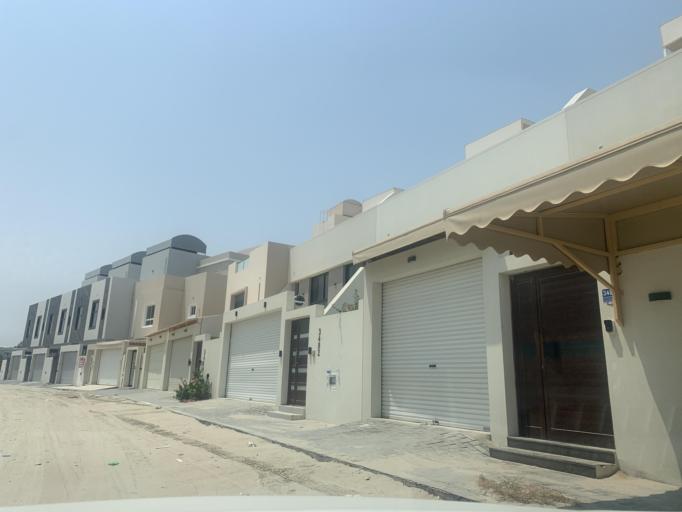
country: BH
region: Central Governorate
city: Madinat Hamad
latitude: 26.1461
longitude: 50.4655
